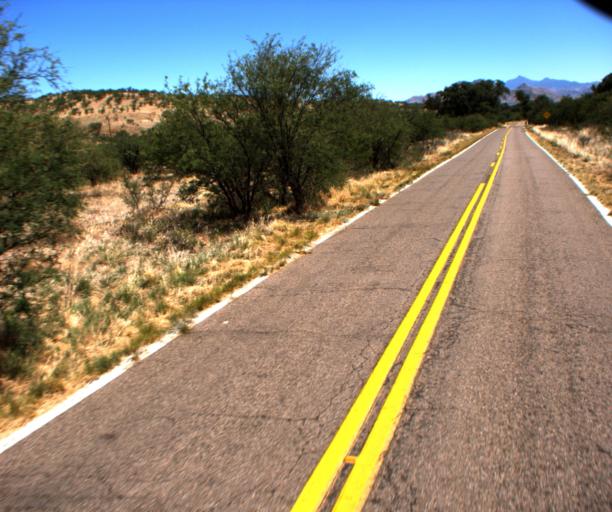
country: US
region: Arizona
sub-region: Santa Cruz County
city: Rio Rico
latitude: 31.4135
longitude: -111.0198
